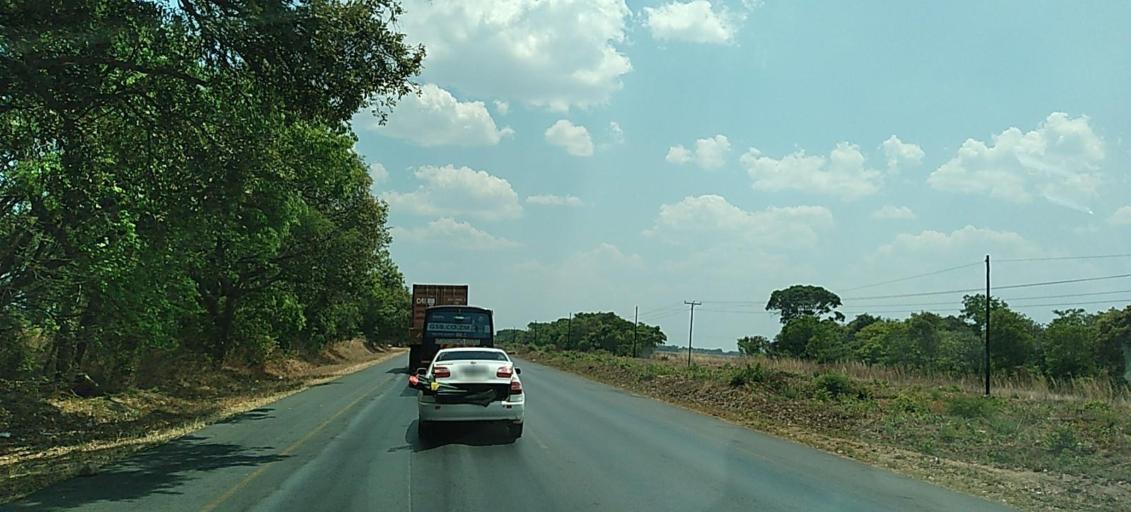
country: ZM
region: Central
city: Kabwe
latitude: -14.3363
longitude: 28.5320
